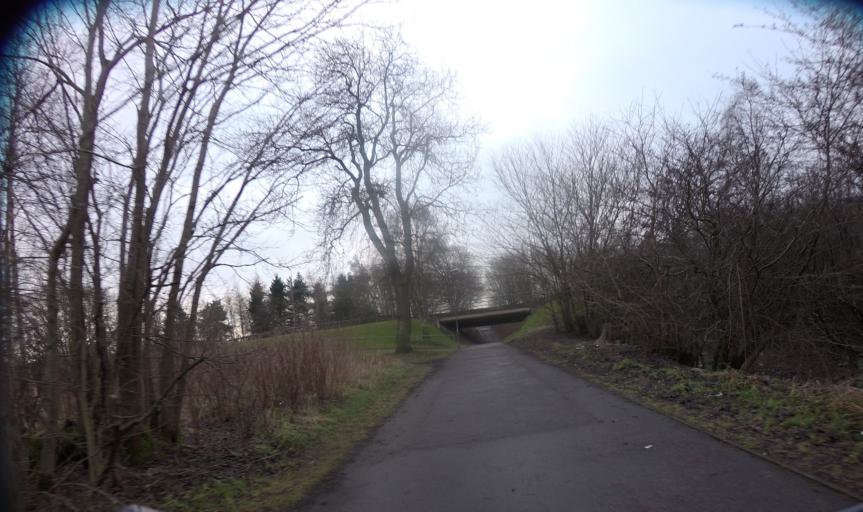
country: GB
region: Scotland
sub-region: West Lothian
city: Livingston
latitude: 55.8702
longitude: -3.5296
